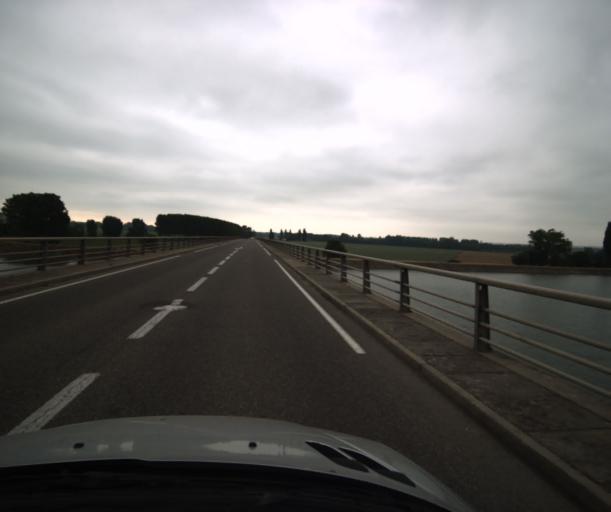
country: FR
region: Midi-Pyrenees
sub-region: Departement du Tarn-et-Garonne
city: Saint-Nicolas-de-la-Grave
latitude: 44.0847
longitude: 0.9864
